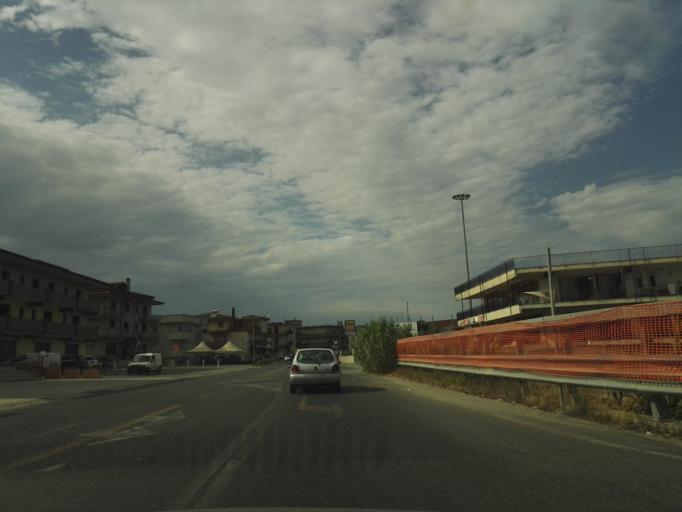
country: IT
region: Calabria
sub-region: Provincia di Catanzaro
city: Marina di Davoli
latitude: 38.6616
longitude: 16.5447
